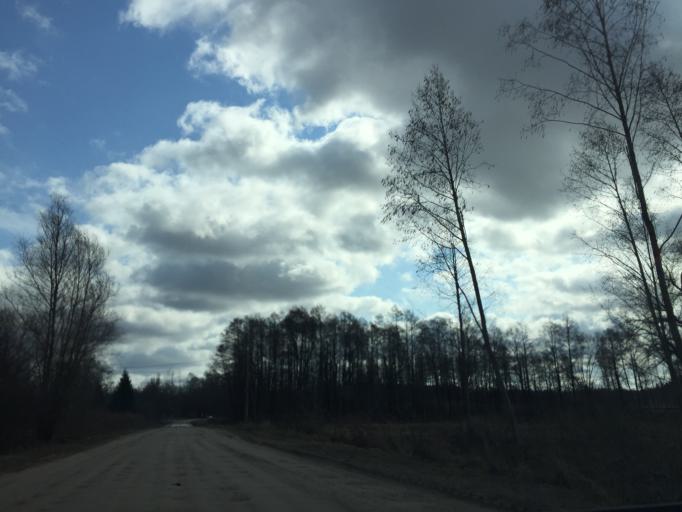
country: LV
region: Vecumnieki
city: Vecumnieki
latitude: 56.5927
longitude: 24.5462
